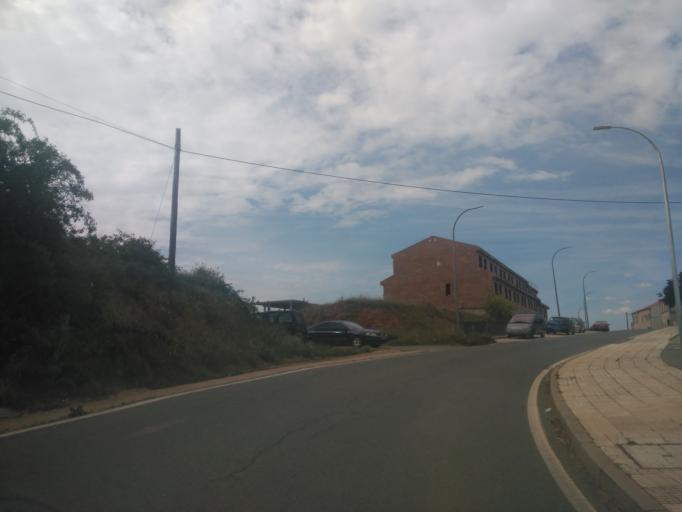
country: ES
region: Castille and Leon
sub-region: Provincia de Salamanca
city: Guijuelo
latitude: 40.5517
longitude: -5.6679
